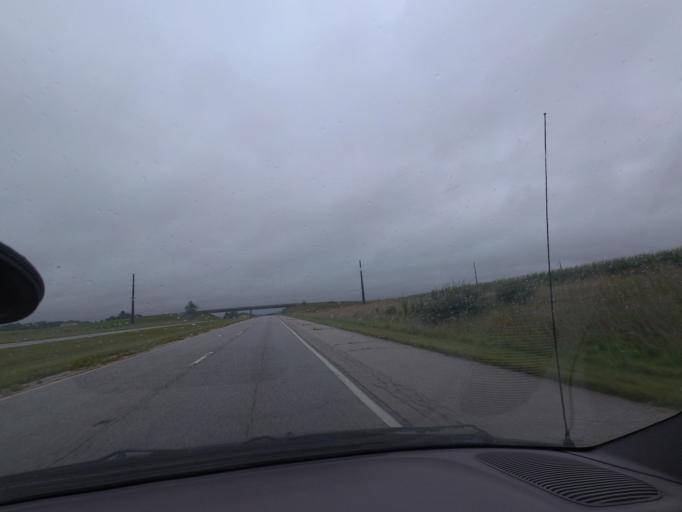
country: US
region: Illinois
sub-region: Pike County
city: Pittsfield
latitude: 39.6711
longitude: -90.8029
